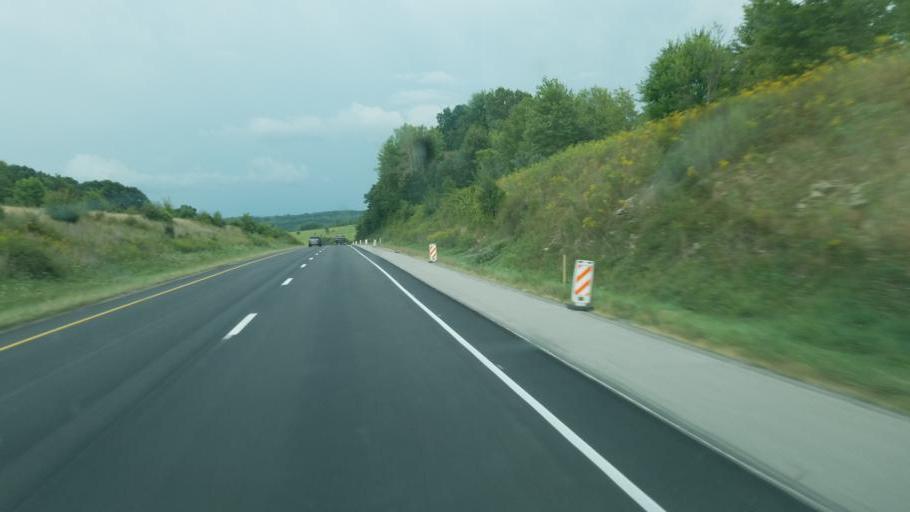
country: US
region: Pennsylvania
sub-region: Venango County
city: Franklin
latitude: 41.1907
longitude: -79.8002
